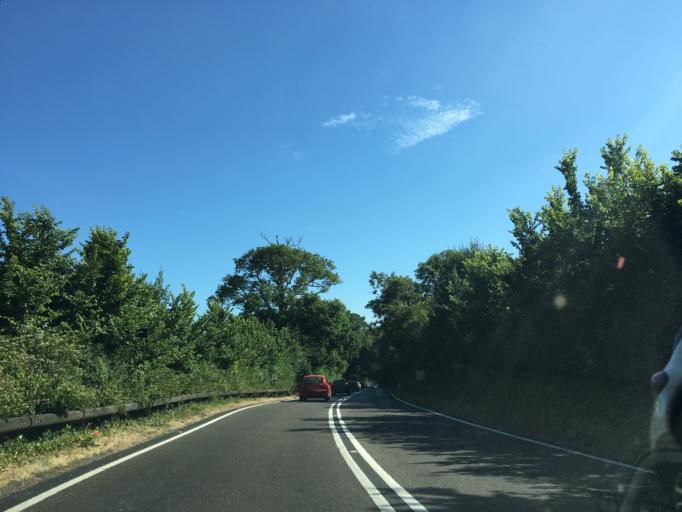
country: GB
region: England
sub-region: Isle of Wight
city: Brading
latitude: 50.6987
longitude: -1.1443
